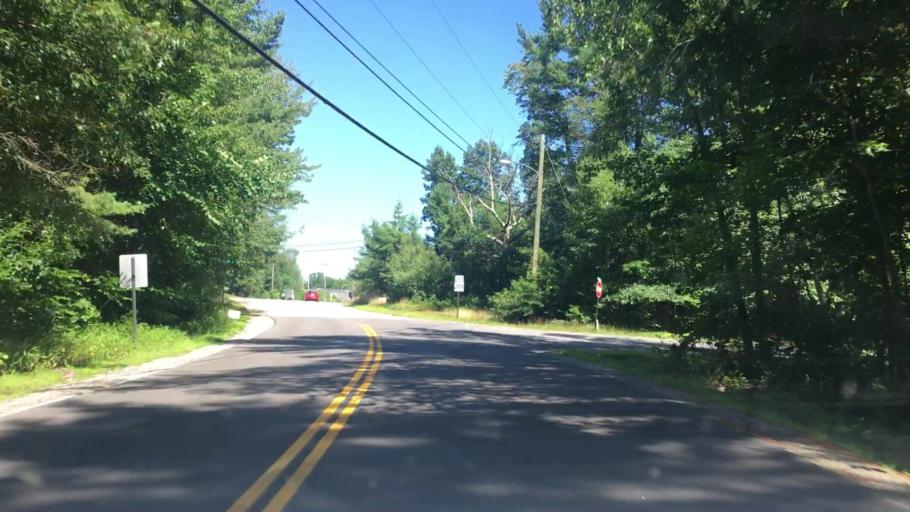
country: US
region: New Hampshire
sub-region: Rockingham County
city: Auburn
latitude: 43.0236
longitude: -71.3707
